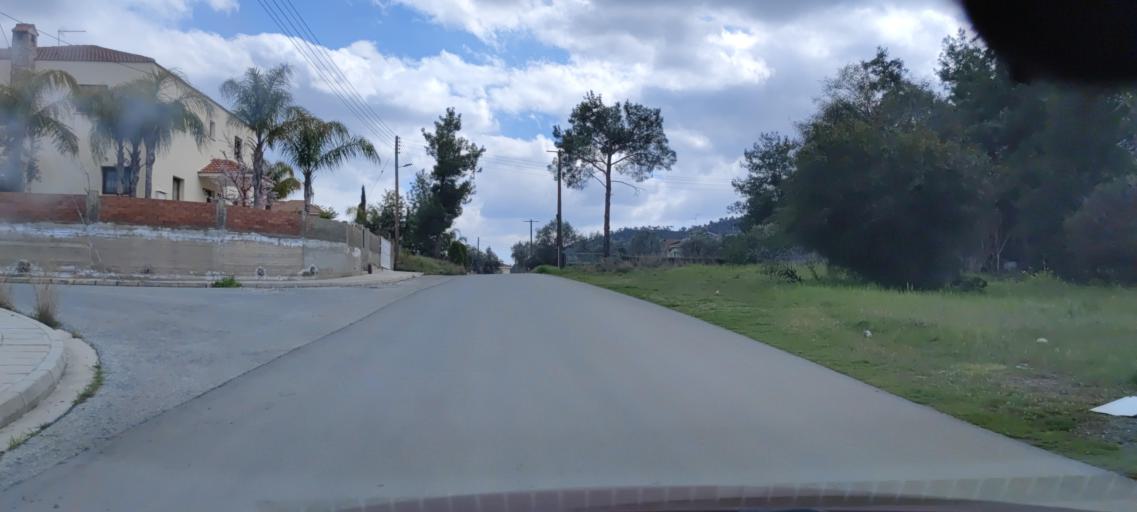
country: CY
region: Lefkosia
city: Lythrodontas
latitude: 34.9466
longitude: 33.3080
